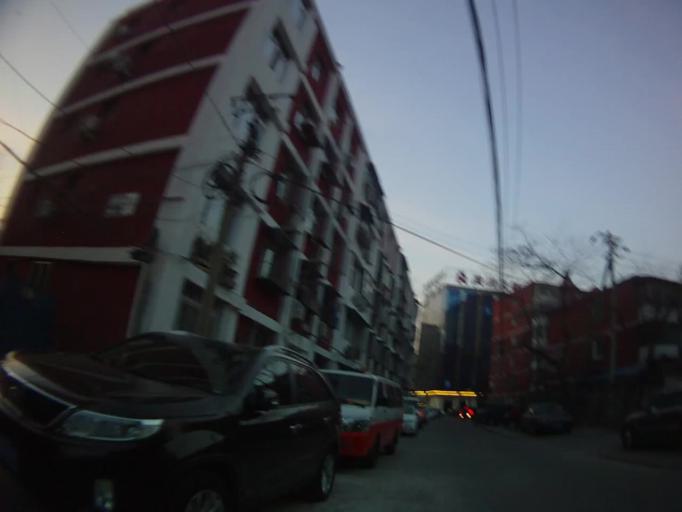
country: CN
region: Beijing
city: Longtan
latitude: 39.8871
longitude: 116.4299
